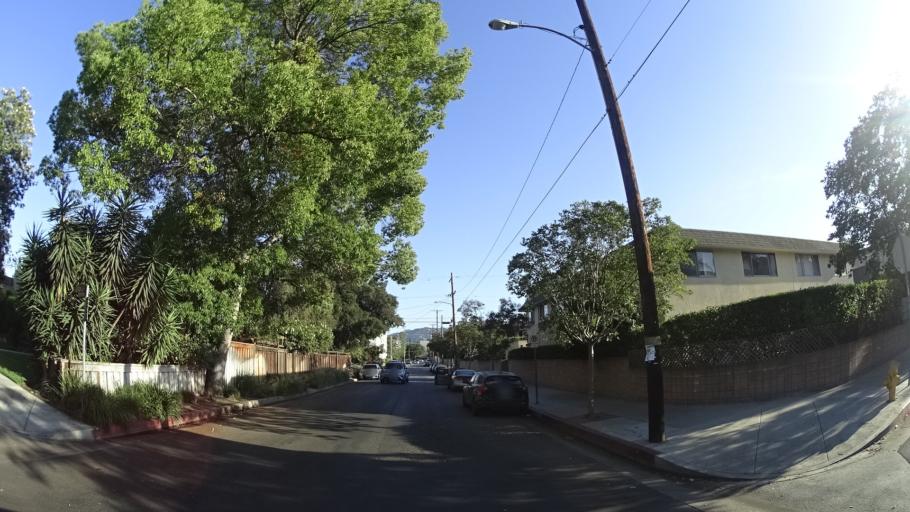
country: US
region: California
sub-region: Los Angeles County
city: North Hollywood
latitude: 34.1600
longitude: -118.3681
